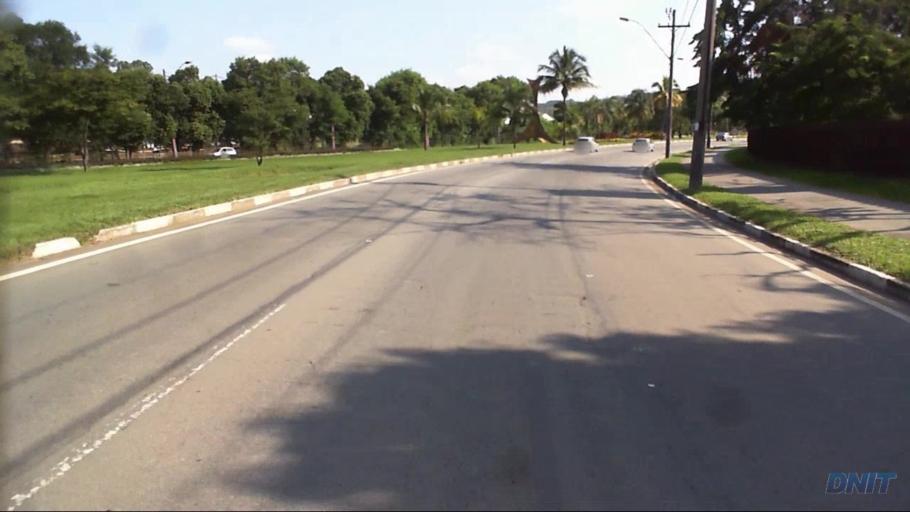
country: BR
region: Minas Gerais
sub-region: Ipatinga
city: Ipatinga
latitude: -19.4854
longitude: -42.5556
